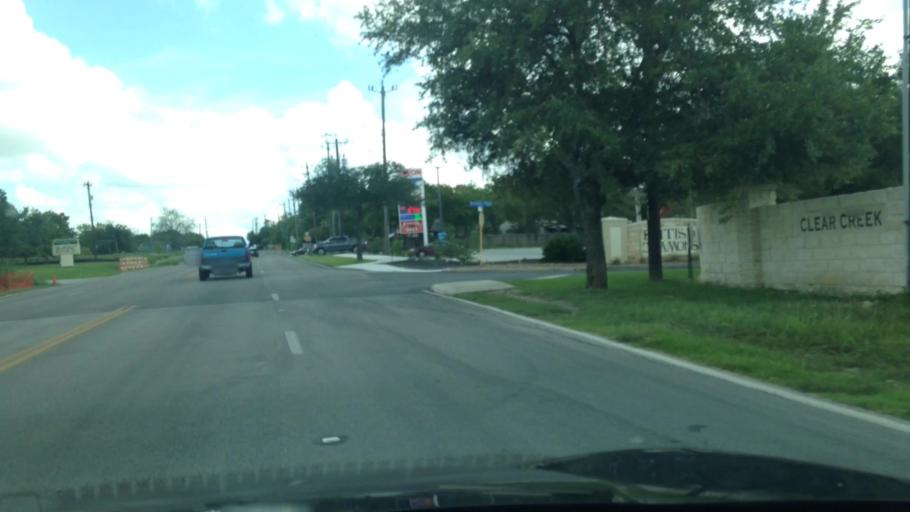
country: US
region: Texas
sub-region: Bexar County
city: Windcrest
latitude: 29.5740
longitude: -98.3984
